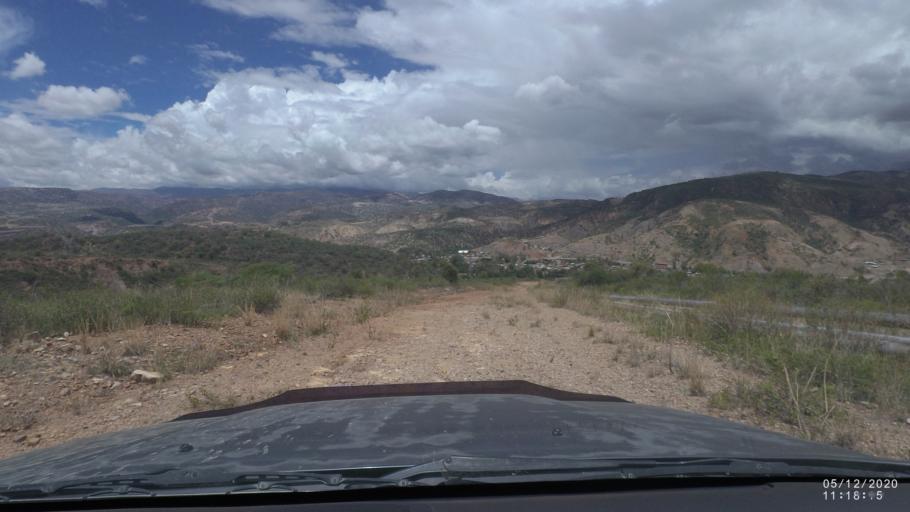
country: BO
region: Cochabamba
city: Sipe Sipe
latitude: -17.5525
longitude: -66.3328
